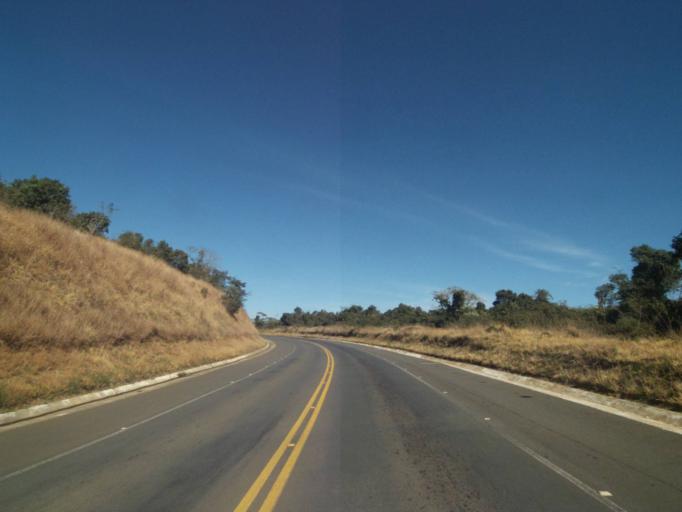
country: BR
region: Parana
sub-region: Tibagi
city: Tibagi
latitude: -24.7557
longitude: -50.4692
